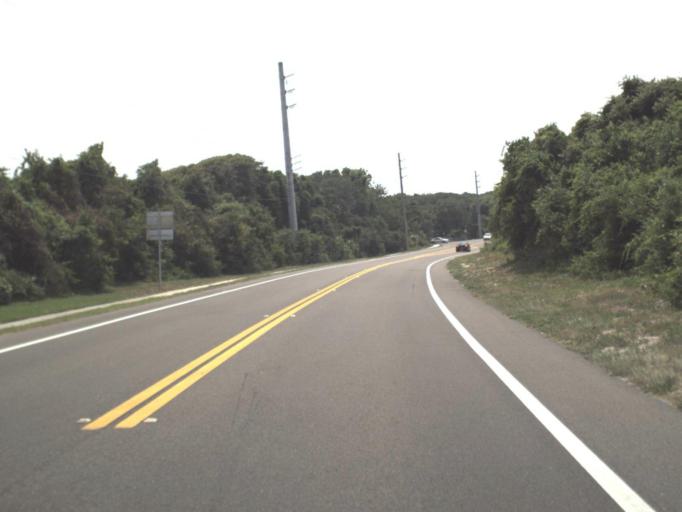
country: US
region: Florida
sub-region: Nassau County
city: Fernandina Beach
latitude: 30.6009
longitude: -81.4446
